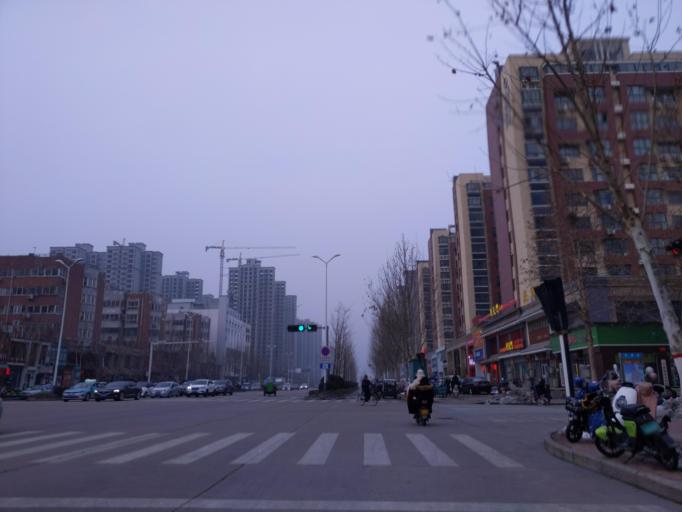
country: CN
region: Henan Sheng
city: Puyang
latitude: 35.7842
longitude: 115.0268
